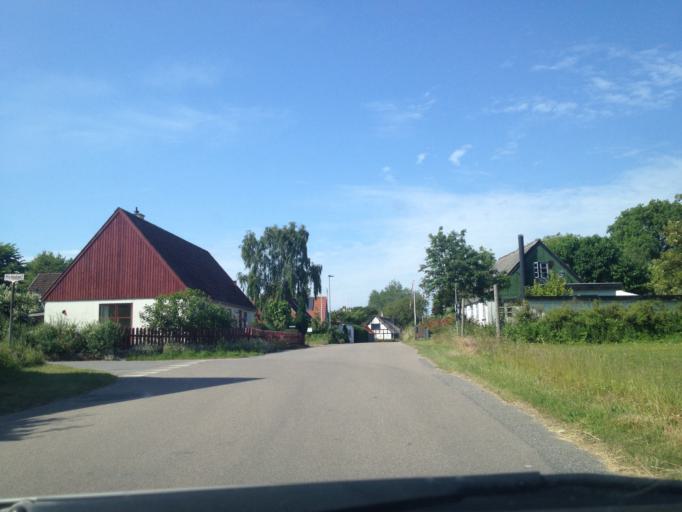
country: DK
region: Central Jutland
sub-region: Samso Kommune
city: Tranebjerg
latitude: 55.8387
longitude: 10.5557
